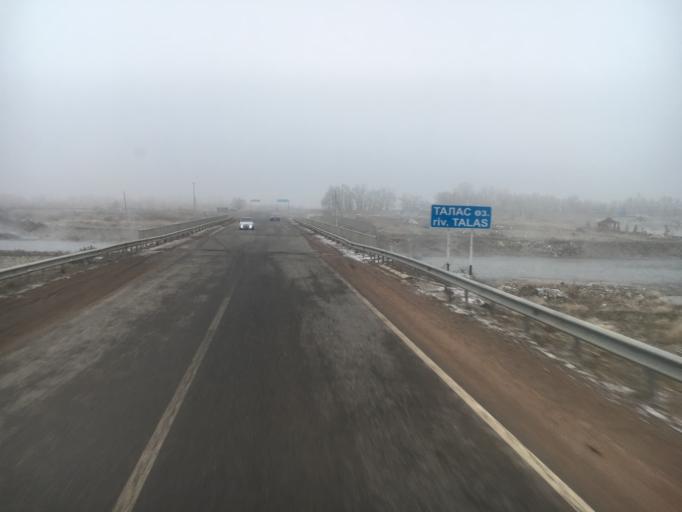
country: KZ
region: Zhambyl
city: Sarykemer
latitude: 43.0402
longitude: 71.5373
